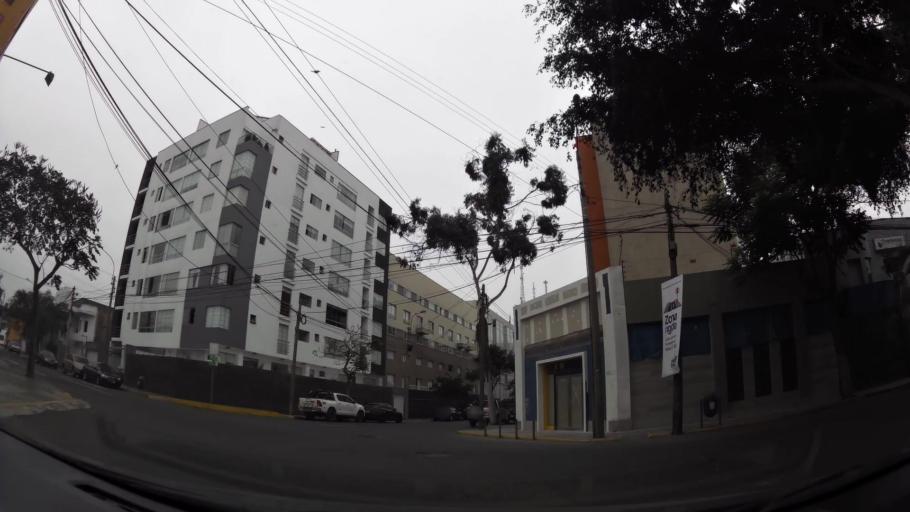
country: PE
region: Lima
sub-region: Lima
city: San Isidro
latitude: -12.1169
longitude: -77.0304
